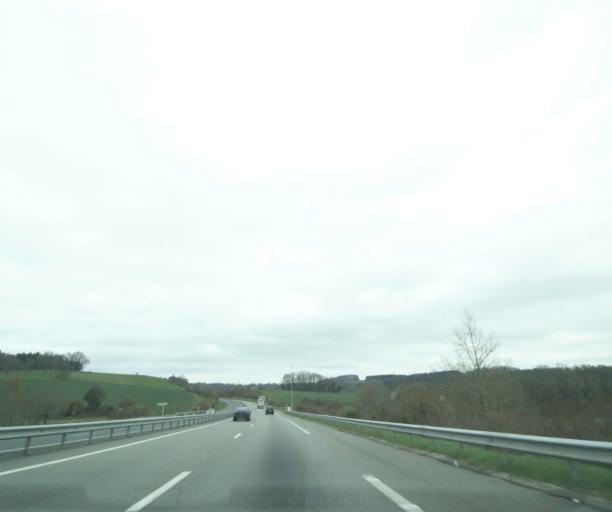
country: FR
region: Limousin
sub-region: Departement de la Correze
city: Vigeois
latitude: 45.4102
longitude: 1.5287
